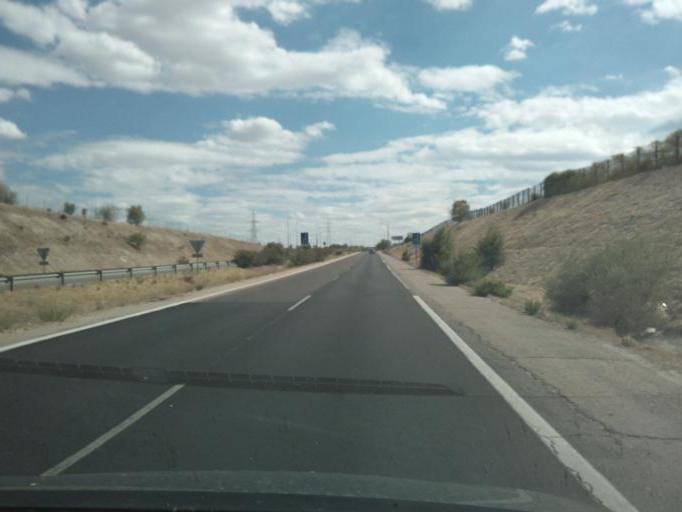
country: ES
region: Madrid
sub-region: Provincia de Madrid
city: San Sebastian de los Reyes
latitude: 40.5580
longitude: -3.6086
